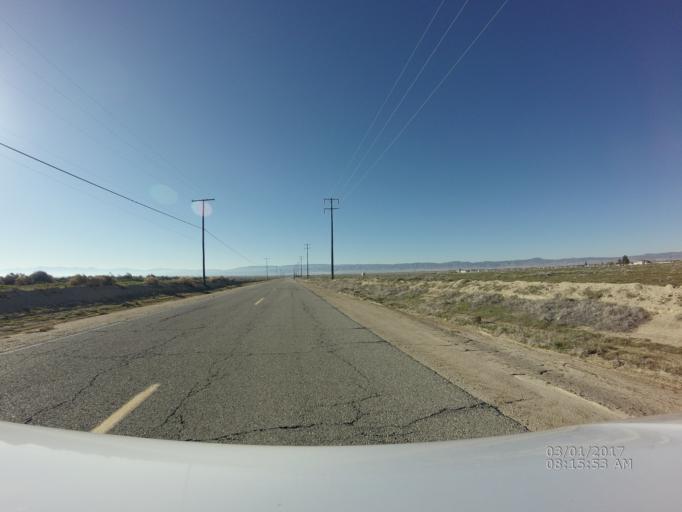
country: US
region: California
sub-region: Los Angeles County
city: Quartz Hill
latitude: 34.7675
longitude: -118.2546
